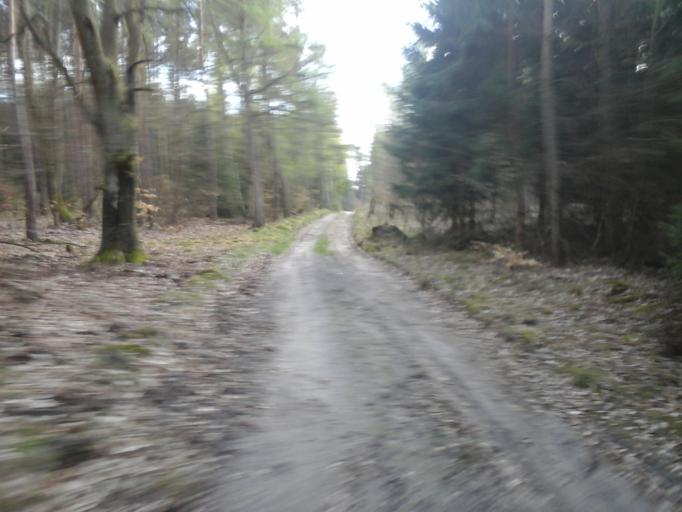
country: PL
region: West Pomeranian Voivodeship
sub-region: Powiat choszczenski
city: Bierzwnik
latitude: 53.0262
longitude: 15.5995
